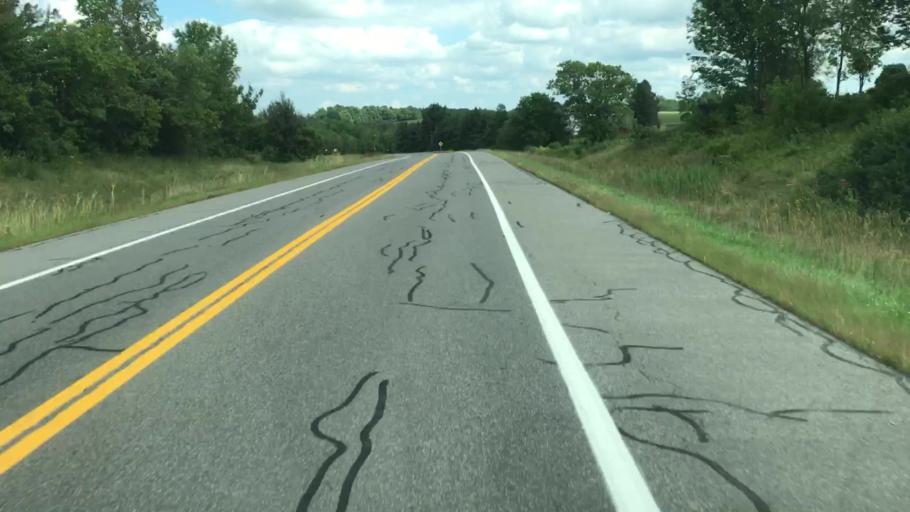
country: US
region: New York
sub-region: Onondaga County
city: Skaneateles
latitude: 42.9481
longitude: -76.3781
